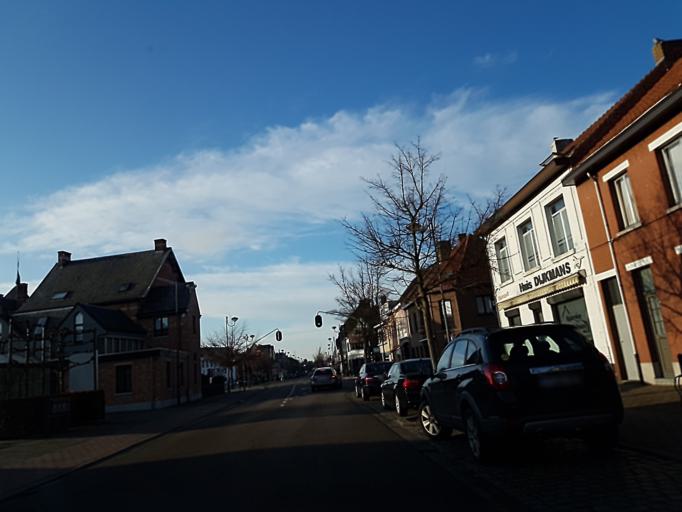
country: BE
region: Flanders
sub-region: Provincie Antwerpen
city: Oud-Turnhout
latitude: 51.3176
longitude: 4.9832
